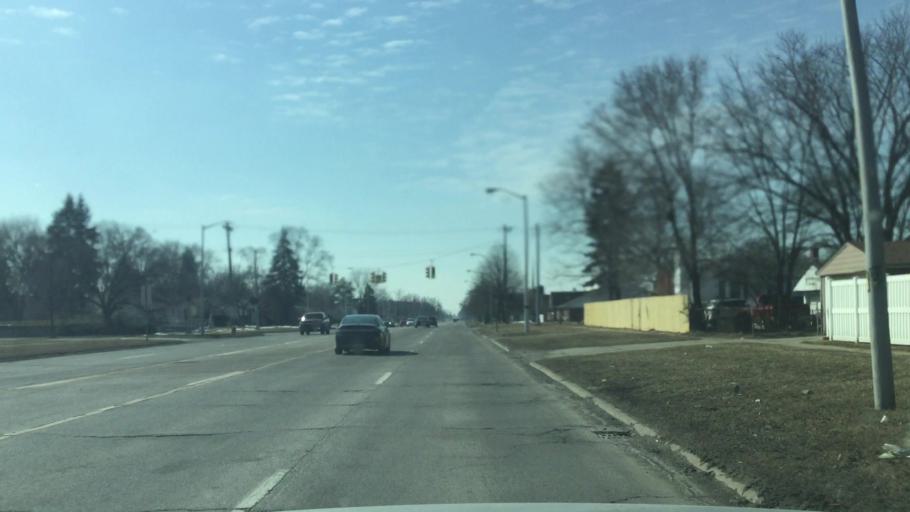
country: US
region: Michigan
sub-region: Wayne County
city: Garden City
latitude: 42.3115
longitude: -83.3200
